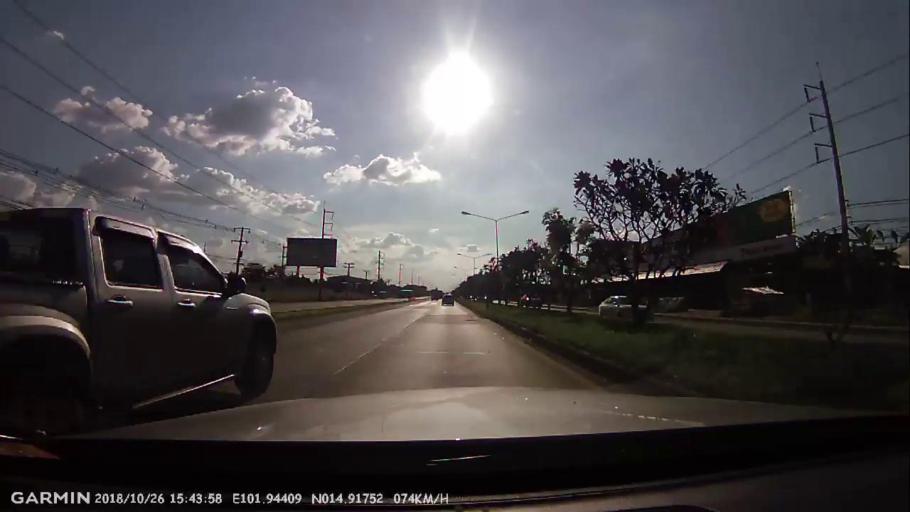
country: TH
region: Nakhon Ratchasima
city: Kham Thale So
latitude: 14.9175
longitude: 101.9442
